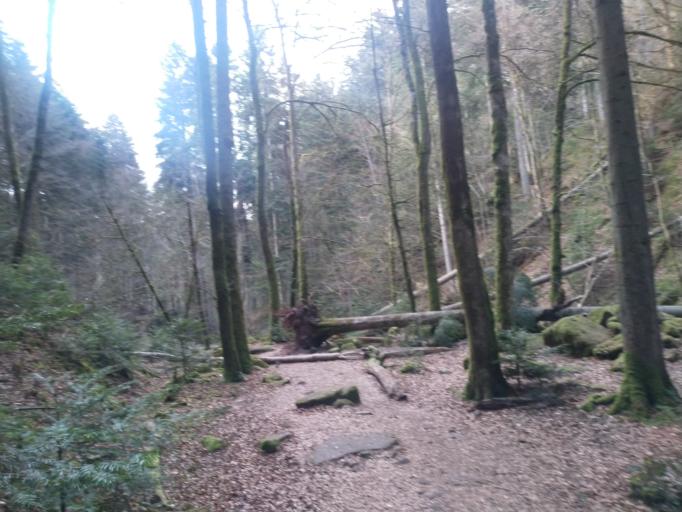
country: DE
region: Baden-Wuerttemberg
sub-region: Karlsruhe Region
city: Bad Liebenzell
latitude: 48.7981
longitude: 8.7451
